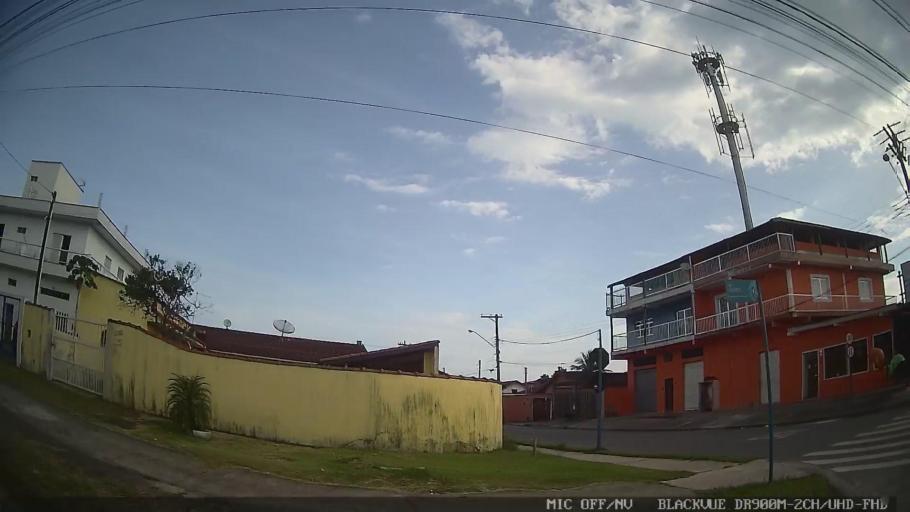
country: BR
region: Sao Paulo
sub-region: Bertioga
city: Bertioga
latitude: -23.8150
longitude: -46.0812
